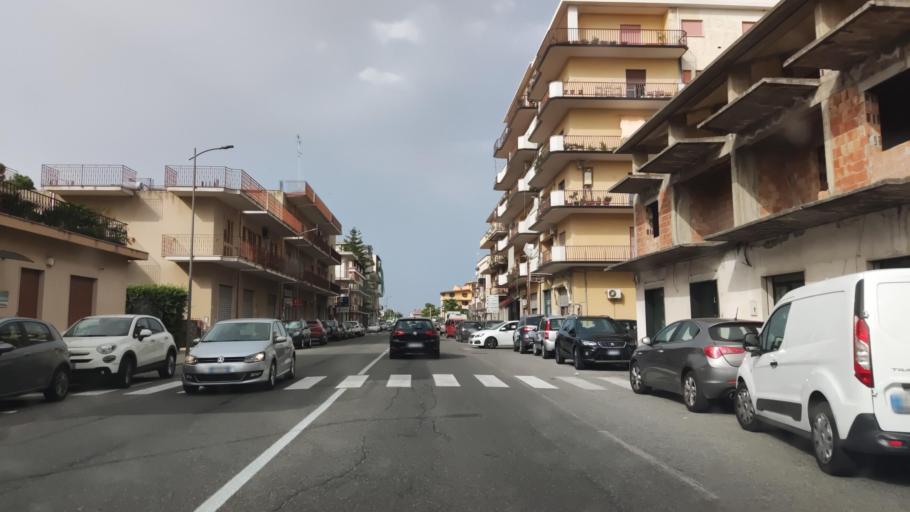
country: IT
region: Calabria
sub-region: Provincia di Reggio Calabria
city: Locri
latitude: 38.2404
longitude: 16.2705
